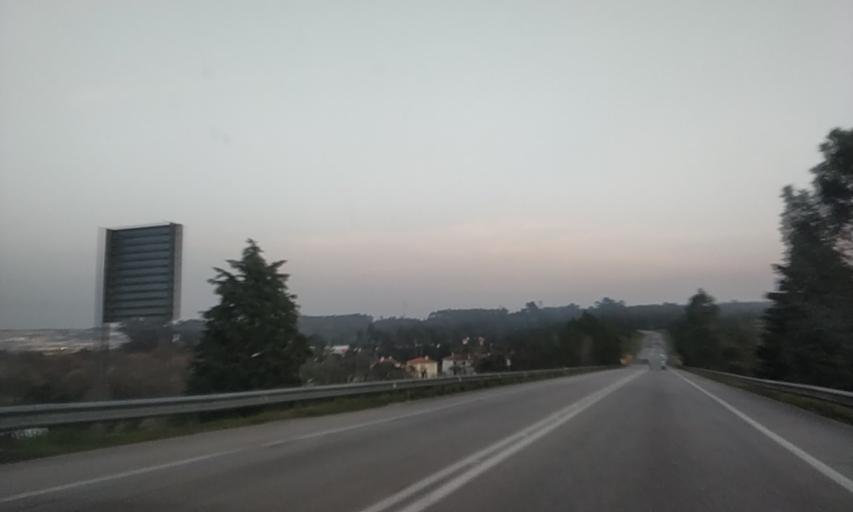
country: PT
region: Leiria
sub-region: Leiria
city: Leiria
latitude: 39.7458
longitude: -8.8514
